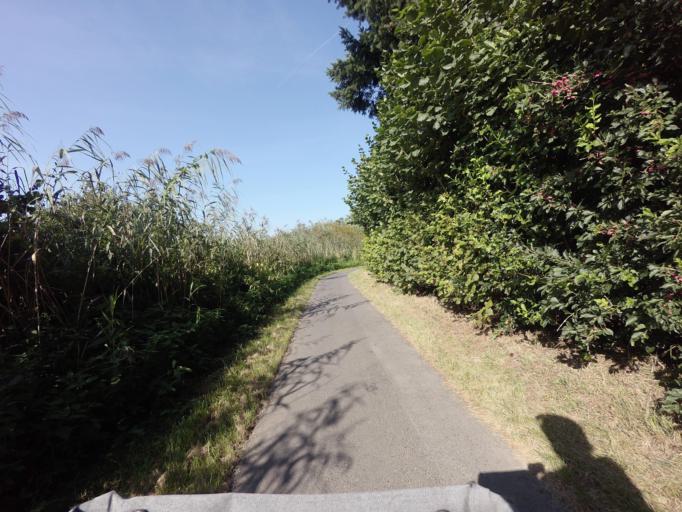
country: DE
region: Lower Saxony
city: Emlichheim
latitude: 52.6027
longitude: 6.8483
